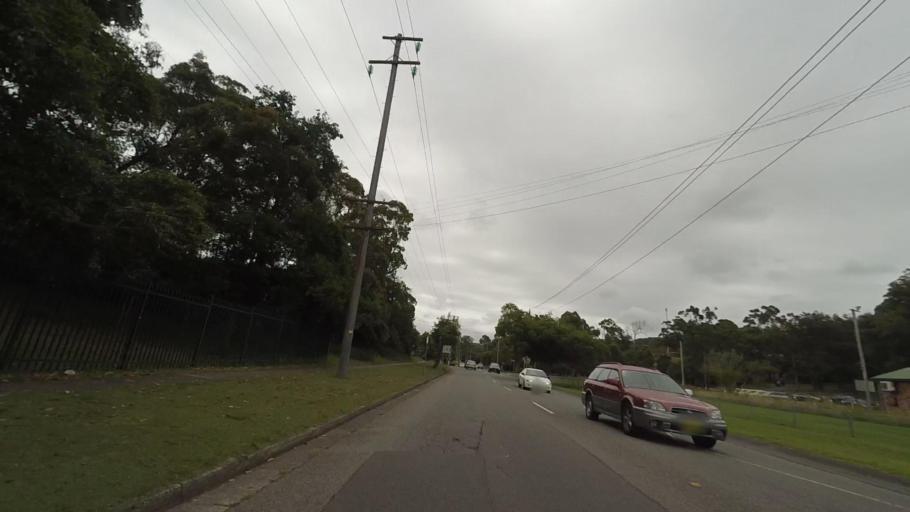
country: AU
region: New South Wales
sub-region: Lake Macquarie Shire
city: Highfields
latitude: -32.9424
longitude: 151.6997
